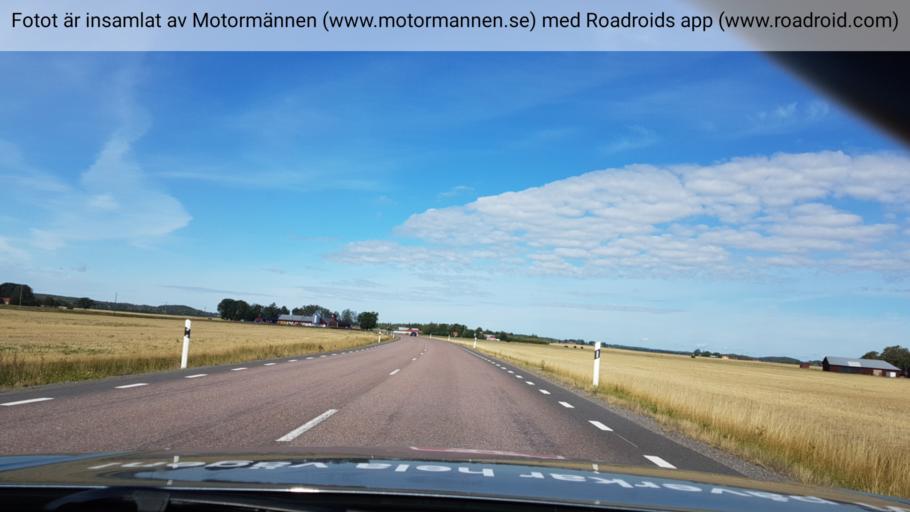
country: SE
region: Uppsala
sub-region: Uppsala Kommun
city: Gamla Uppsala
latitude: 59.9123
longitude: 17.5305
